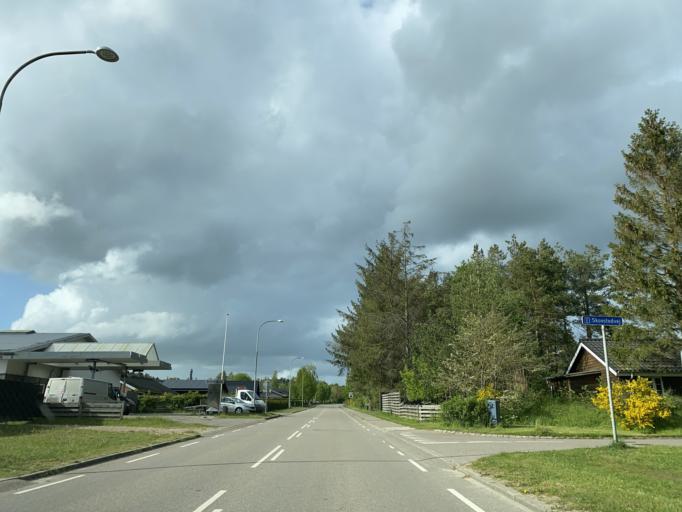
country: DK
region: Central Jutland
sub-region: Skanderborg Kommune
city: Ry
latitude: 56.0655
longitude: 9.6934
